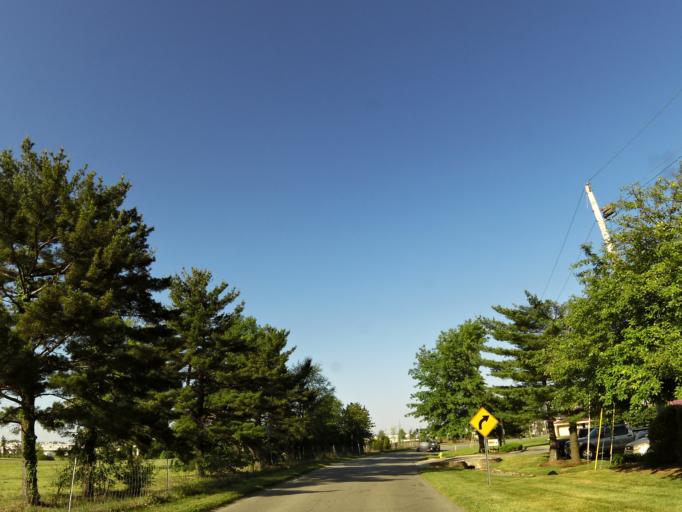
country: US
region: Indiana
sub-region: Jackson County
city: Seymour
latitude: 38.9597
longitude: -85.8460
